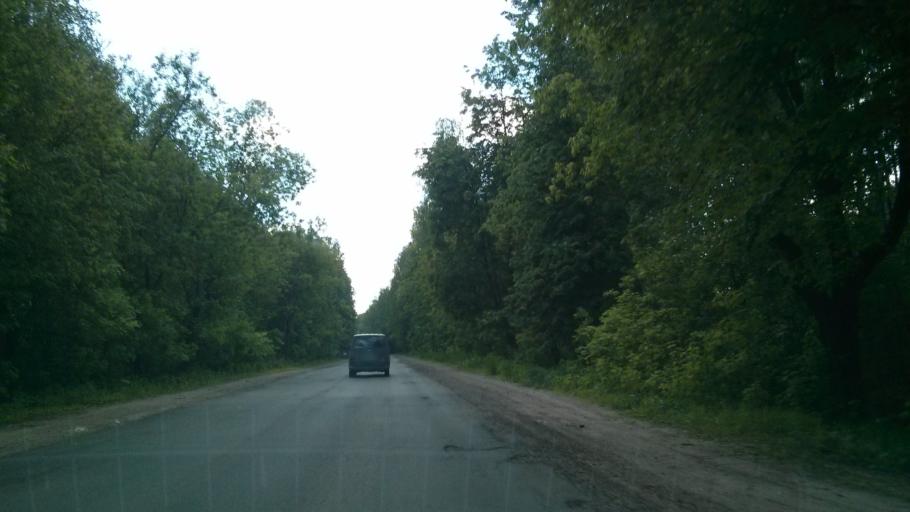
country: RU
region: Vladimir
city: Murom
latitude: 55.5431
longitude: 41.9855
